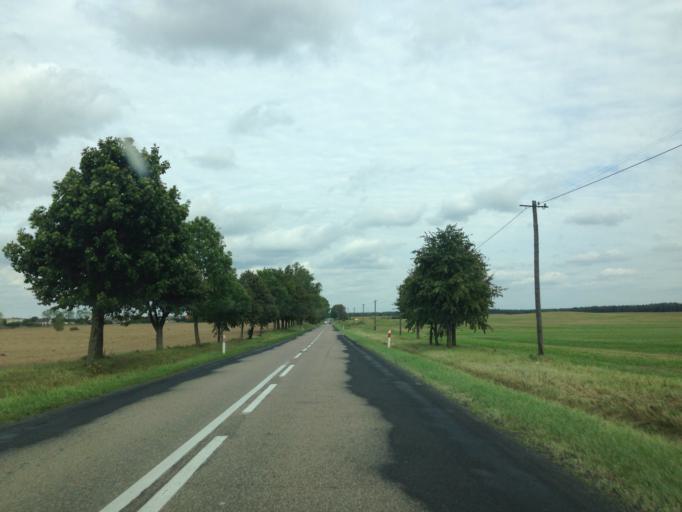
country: PL
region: Warmian-Masurian Voivodeship
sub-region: Powiat dzialdowski
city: Lidzbark
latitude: 53.2630
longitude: 19.7646
